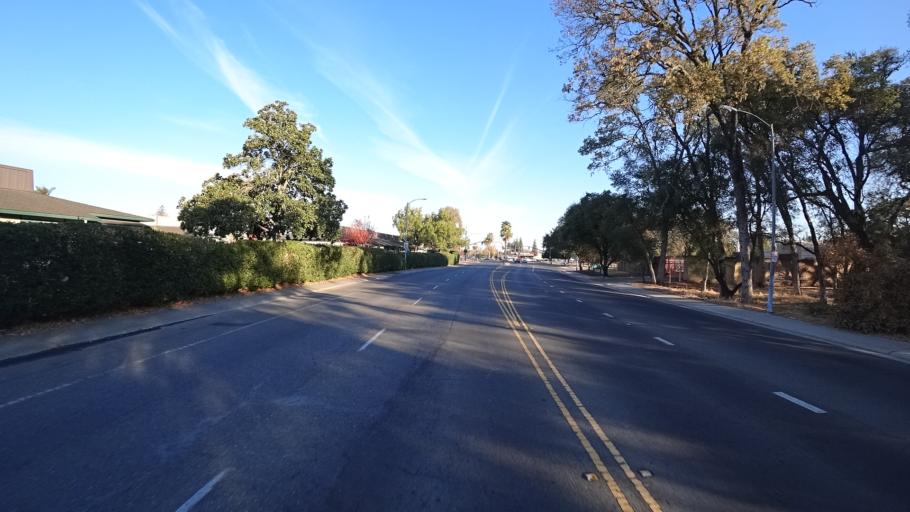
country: US
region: California
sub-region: Sacramento County
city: Antelope
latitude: 38.6855
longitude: -121.3089
